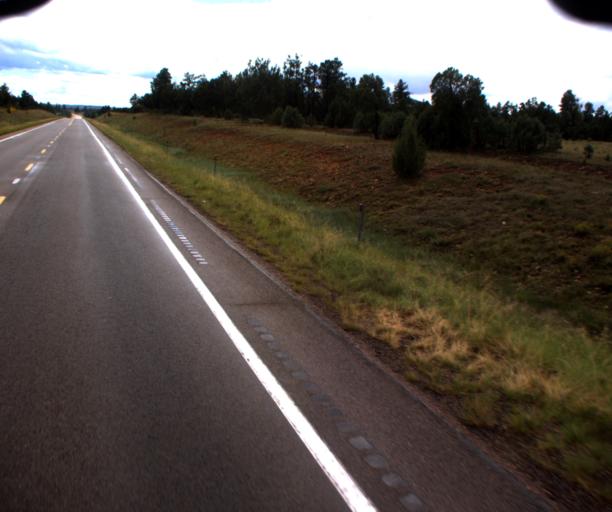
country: US
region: Arizona
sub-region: Navajo County
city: Heber-Overgaard
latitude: 34.3767
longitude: -110.4656
